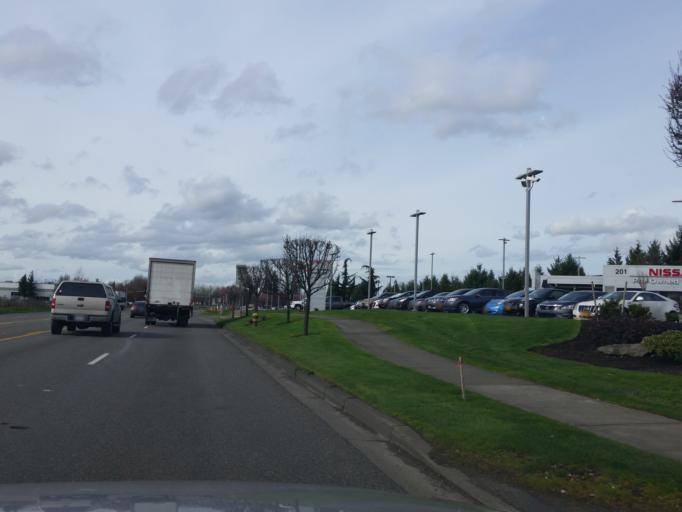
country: US
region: Washington
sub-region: Pierce County
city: North Puyallup
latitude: 47.2072
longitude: -122.2963
